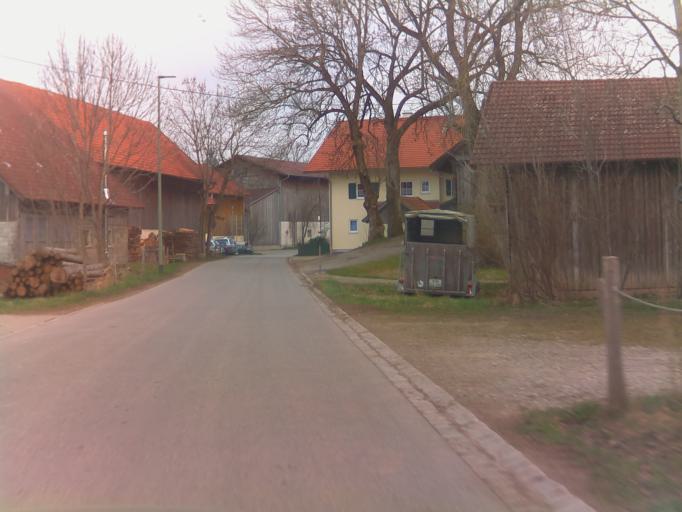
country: DE
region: Bavaria
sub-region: Upper Bavaria
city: Ingenried
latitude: 47.8173
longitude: 10.7804
